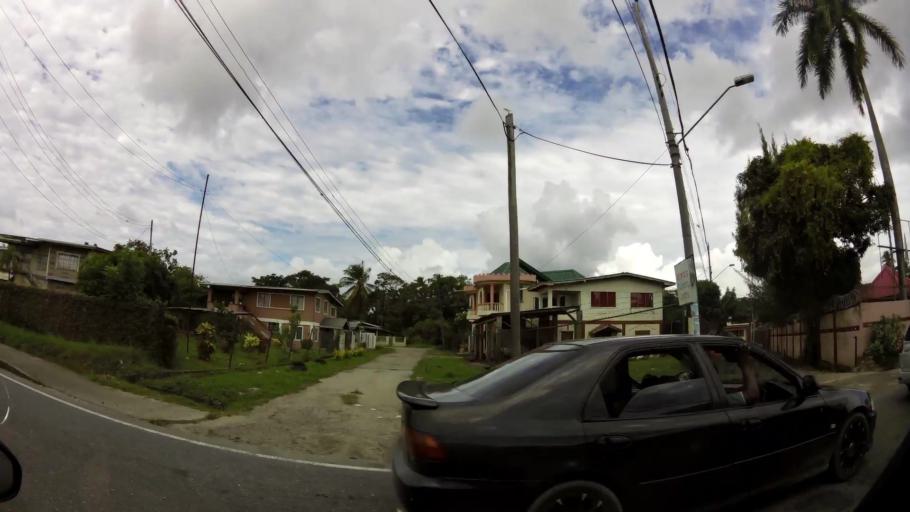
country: TT
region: Couva-Tabaquite-Talparo
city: Couva
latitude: 10.4450
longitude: -61.4481
